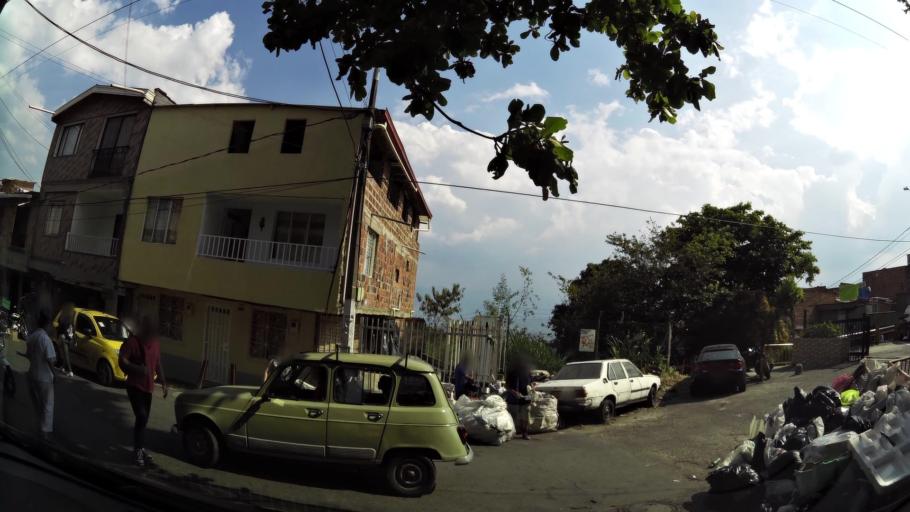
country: CO
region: Antioquia
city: Medellin
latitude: 6.2838
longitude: -75.5938
